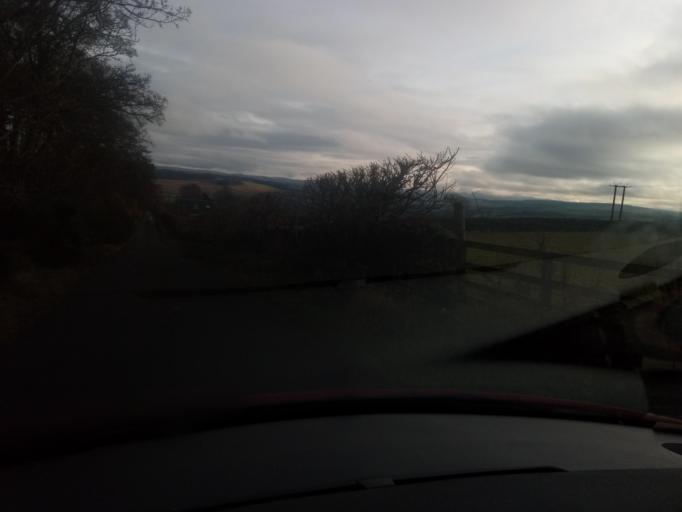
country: GB
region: Scotland
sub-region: The Scottish Borders
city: Jedburgh
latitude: 55.4796
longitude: -2.5707
